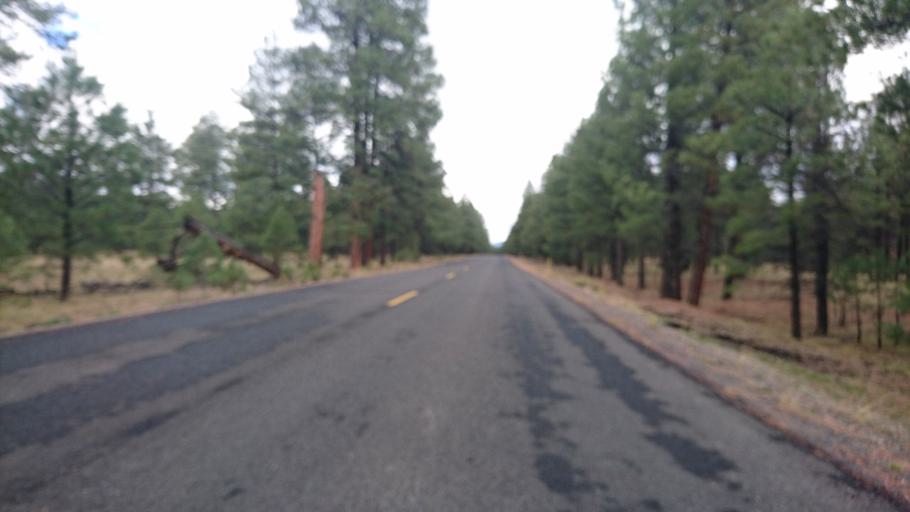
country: US
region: Arizona
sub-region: Coconino County
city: Parks
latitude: 35.2578
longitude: -111.8673
